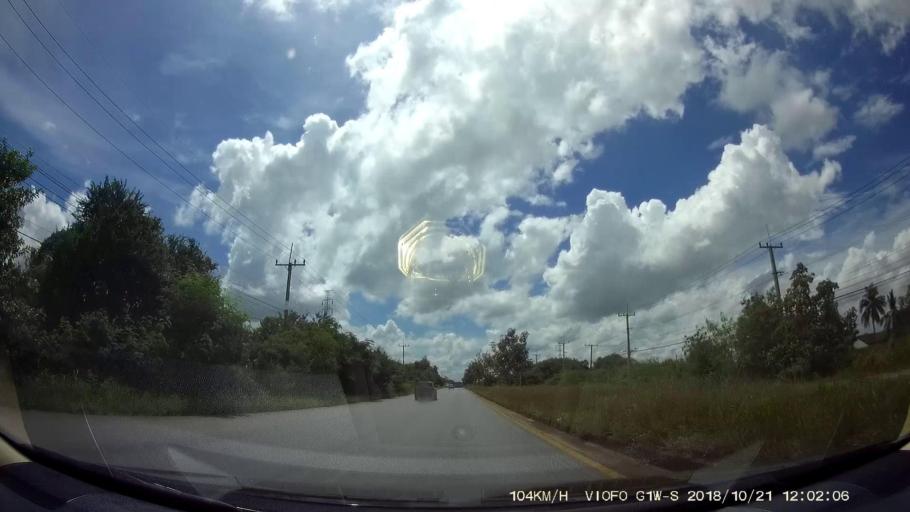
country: TH
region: Chaiyaphum
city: Chatturat
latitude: 15.5293
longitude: 101.8307
